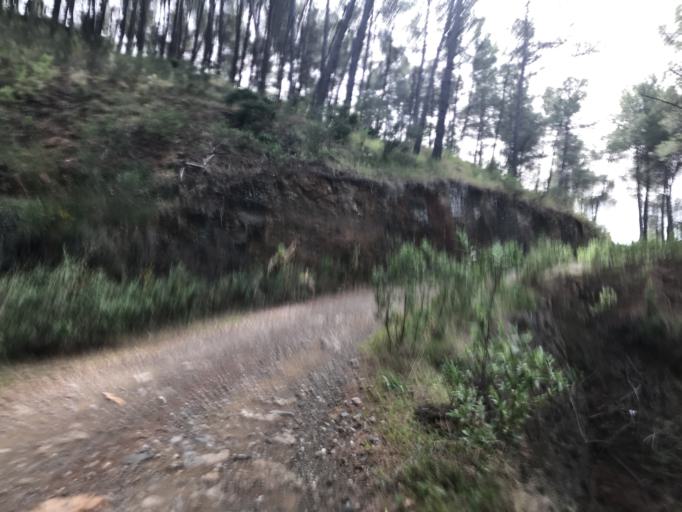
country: ES
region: Andalusia
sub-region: Provincia de Malaga
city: Malaga
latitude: 36.8041
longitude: -4.3991
